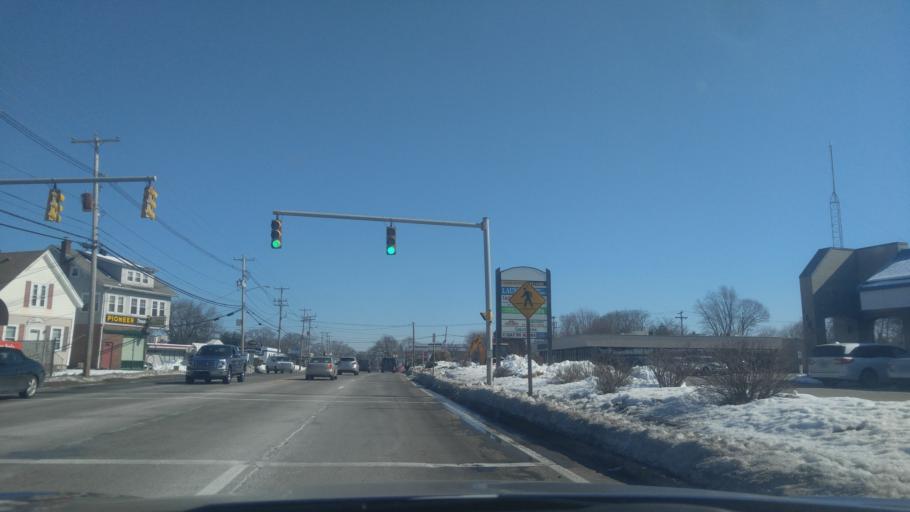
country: US
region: Rhode Island
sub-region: Providence County
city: Cranston
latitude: 41.7470
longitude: -71.4253
